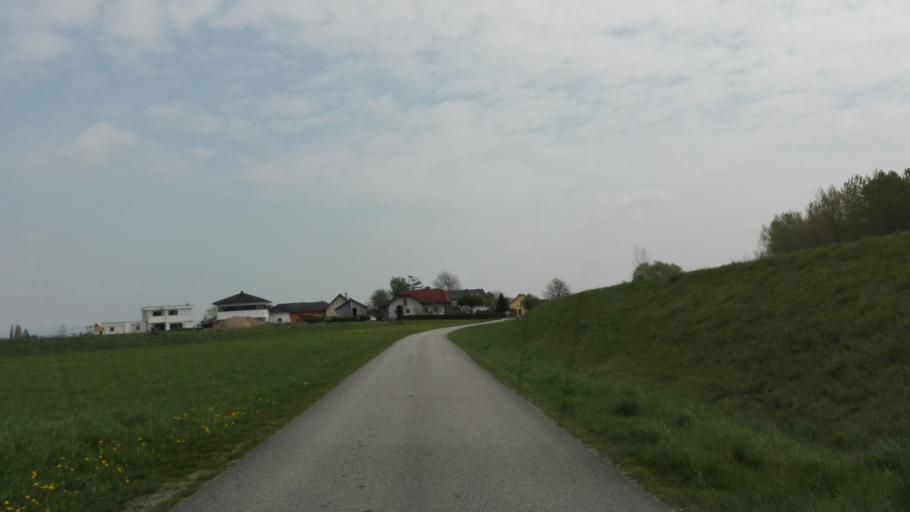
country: AT
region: Lower Austria
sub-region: Politischer Bezirk Amstetten
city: Strengberg
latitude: 48.1819
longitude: 14.6631
